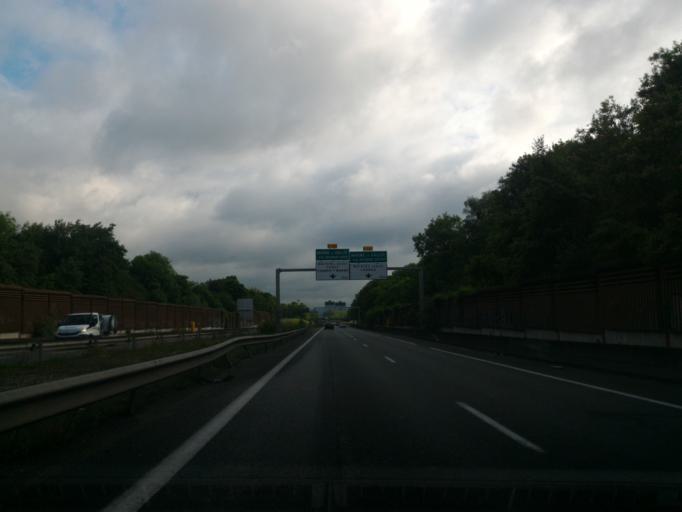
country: FR
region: Ile-de-France
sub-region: Departement de Seine-et-Marne
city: Lognes
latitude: 48.8347
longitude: 2.6225
